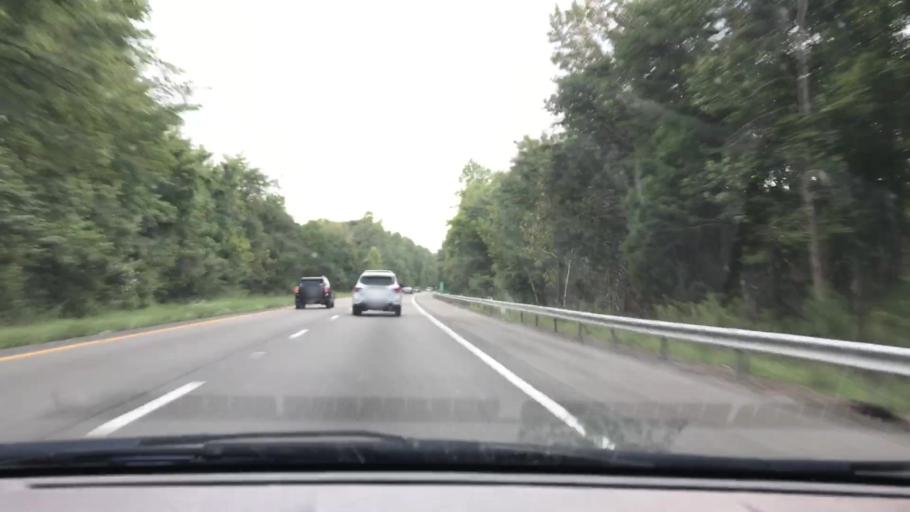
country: US
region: Virginia
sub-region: Goochland County
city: Goochland
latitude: 37.7190
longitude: -77.8095
